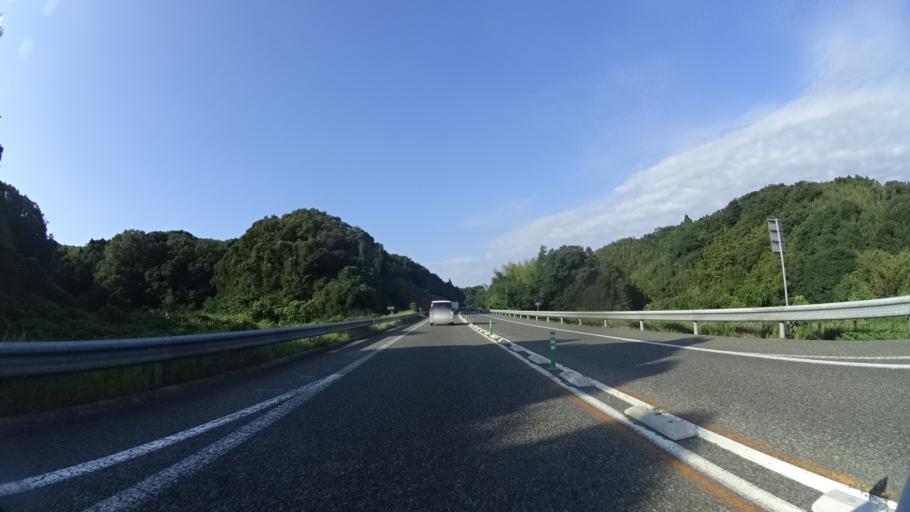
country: JP
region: Shimane
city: Hiratacho
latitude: 35.4016
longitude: 132.9271
